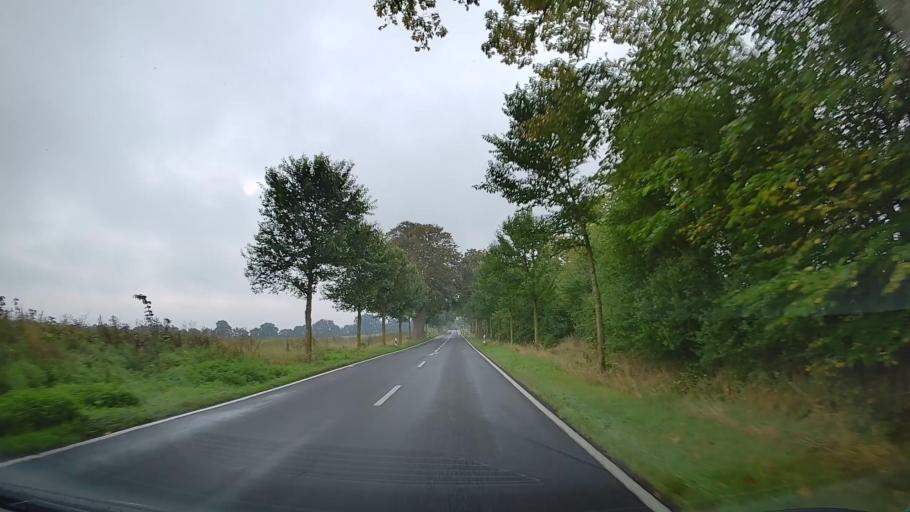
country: DE
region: Mecklenburg-Vorpommern
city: Ostseebad Boltenhagen
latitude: 53.9456
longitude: 11.2358
